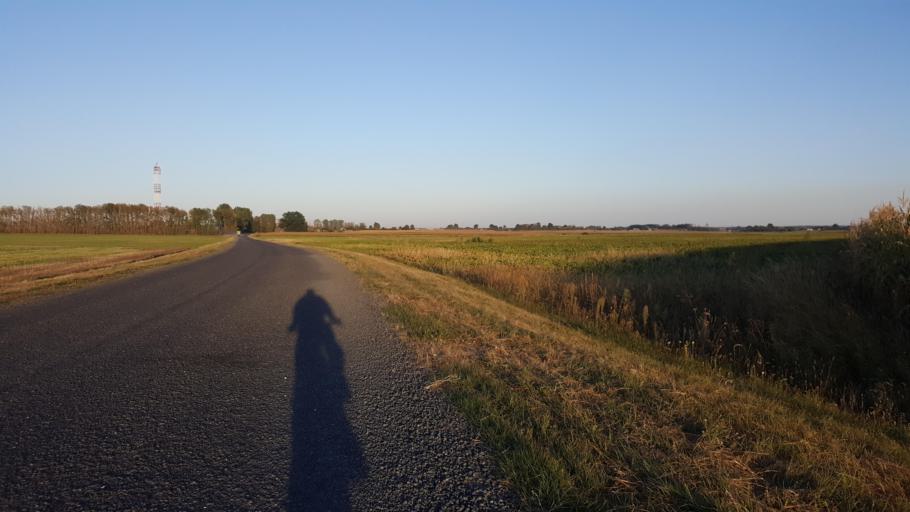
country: BY
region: Brest
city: Vysokaye
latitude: 52.2972
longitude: 23.5053
